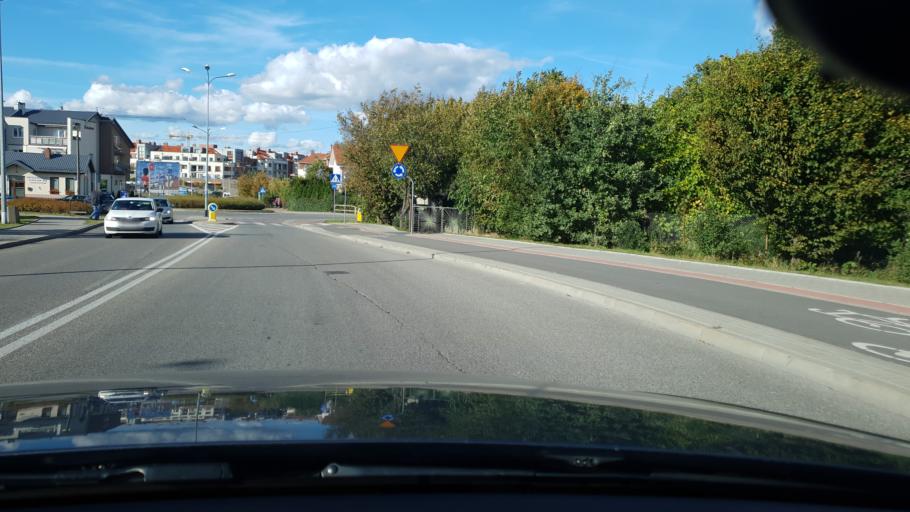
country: PL
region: Pomeranian Voivodeship
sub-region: Powiat kartuski
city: Chwaszczyno
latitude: 54.4978
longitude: 18.4390
